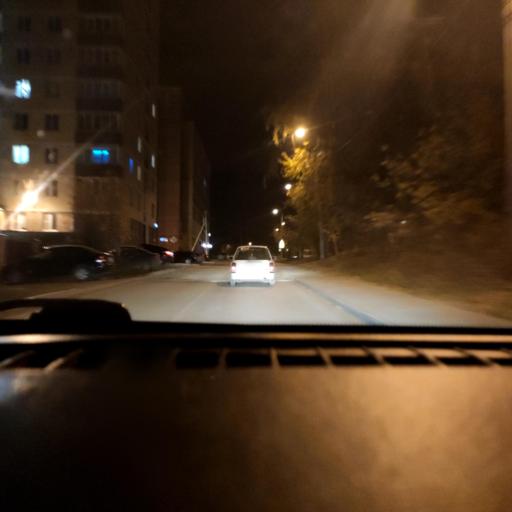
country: RU
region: Perm
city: Perm
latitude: 57.9893
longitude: 56.2225
